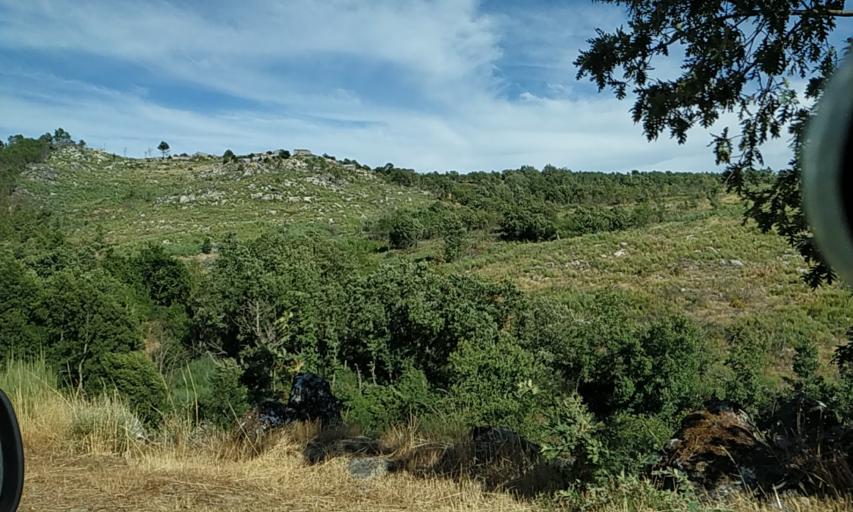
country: PT
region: Vila Real
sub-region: Murca
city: Murca
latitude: 41.3714
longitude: -7.5304
